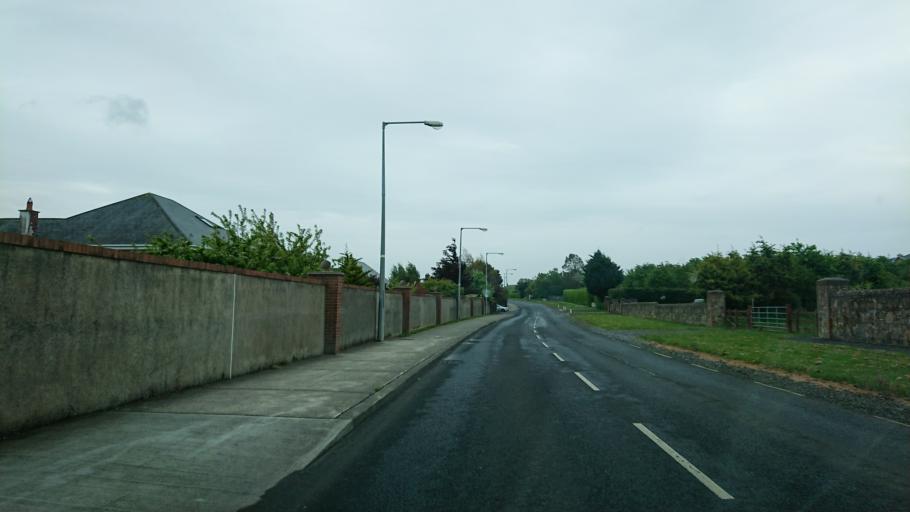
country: IE
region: Munster
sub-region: Waterford
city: Waterford
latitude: 52.2316
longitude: -7.0689
